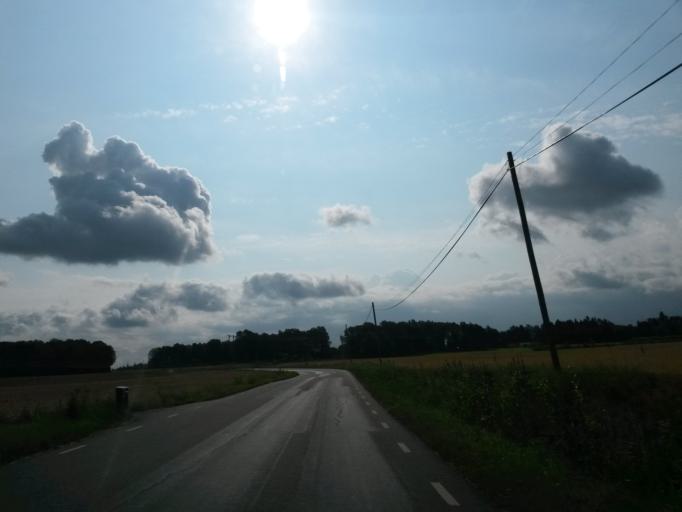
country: SE
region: Vaestra Goetaland
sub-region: Vargarda Kommun
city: Jonstorp
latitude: 58.0044
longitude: 12.7187
